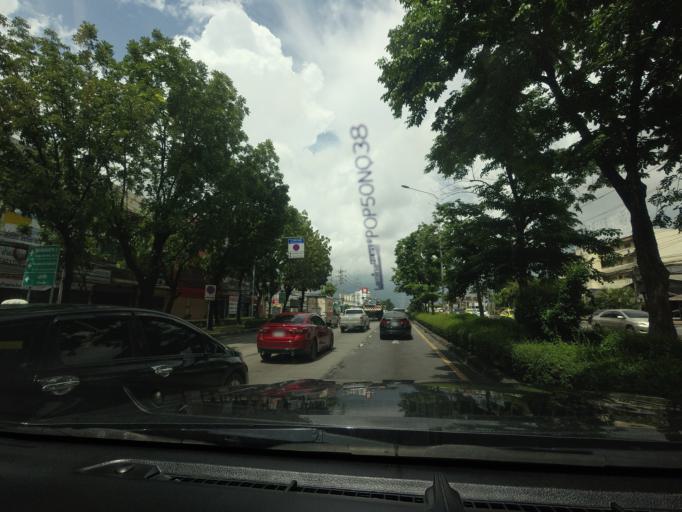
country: TH
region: Bangkok
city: Nong Khaem
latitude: 13.7078
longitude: 100.3751
